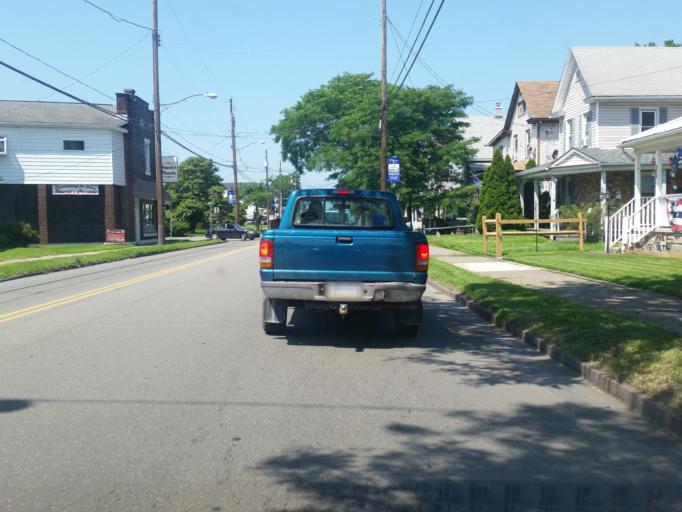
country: US
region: Pennsylvania
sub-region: Columbia County
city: Berwick
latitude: 41.0505
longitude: -76.2467
